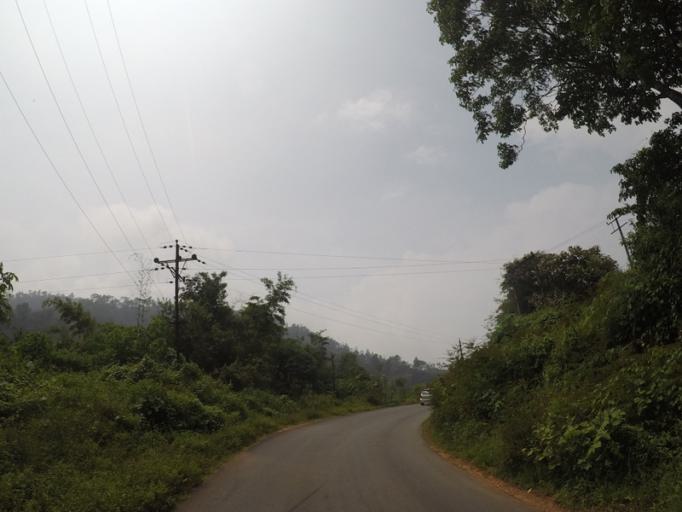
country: IN
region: Karnataka
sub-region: Chikmagalur
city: Mudigere
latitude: 13.1665
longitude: 75.4582
